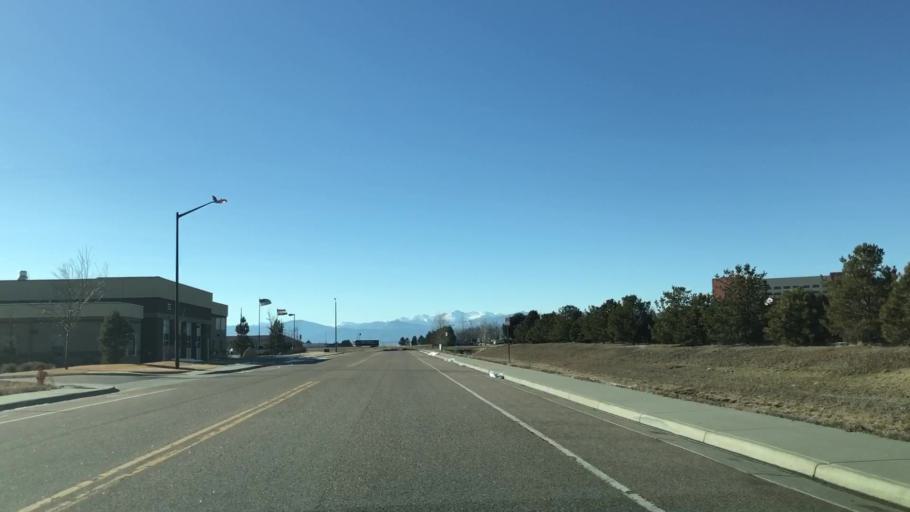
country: US
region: Colorado
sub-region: Weld County
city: Windsor
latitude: 40.4391
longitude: -104.9860
